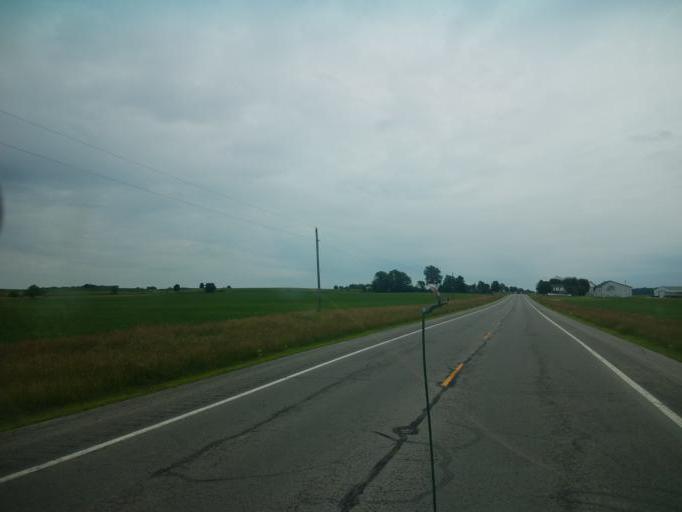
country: US
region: Ohio
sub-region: Hardin County
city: Kenton
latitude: 40.6954
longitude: -83.7074
